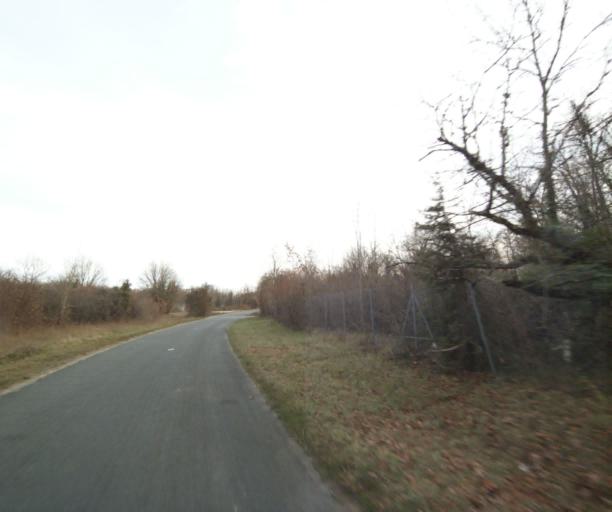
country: FR
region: Poitou-Charentes
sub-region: Departement de la Charente-Maritime
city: Fontcouverte
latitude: 45.8068
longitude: -0.5813
